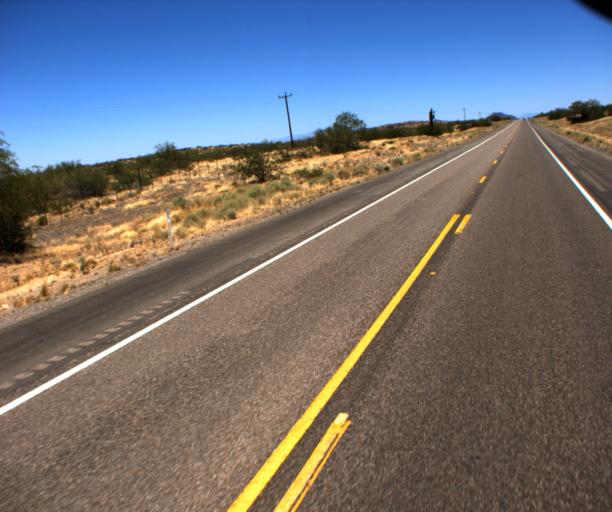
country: US
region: Arizona
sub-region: Pima County
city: Sells
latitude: 32.0210
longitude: -111.6071
